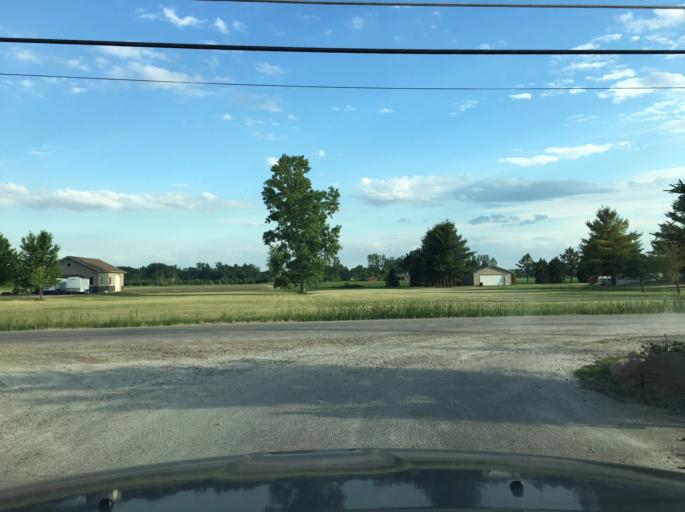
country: US
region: Michigan
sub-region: Macomb County
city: Romeo
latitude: 42.7897
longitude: -82.9592
